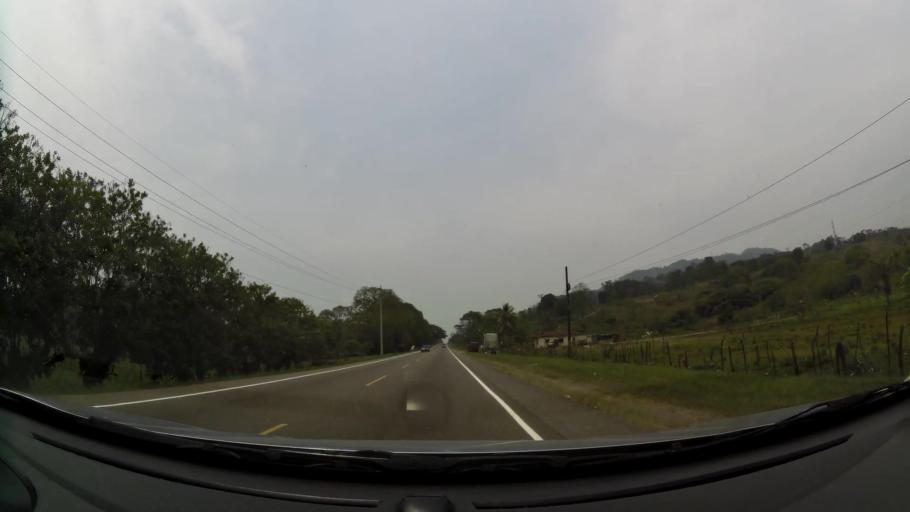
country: HN
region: Cortes
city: La Guama
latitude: 14.8287
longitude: -87.9608
